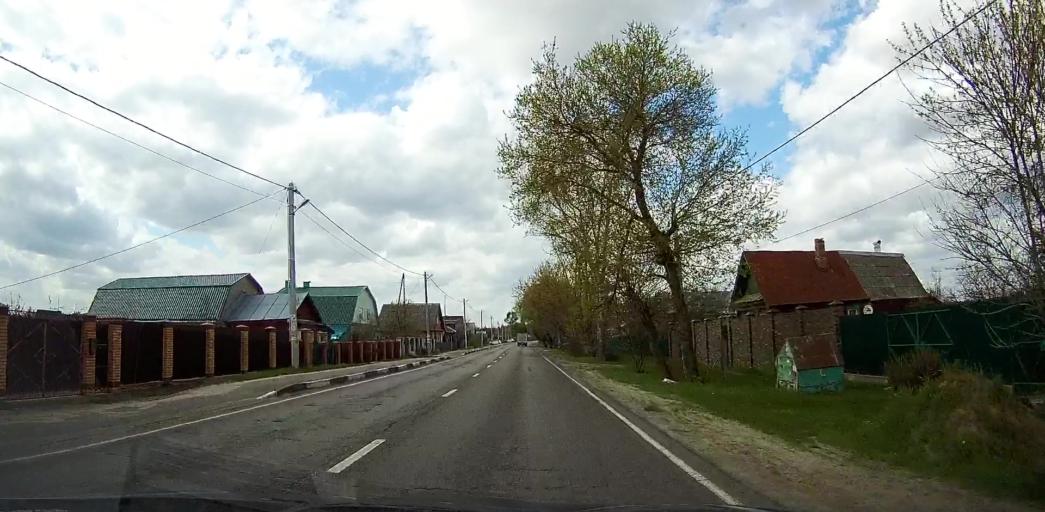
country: RU
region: Moskovskaya
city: Davydovo
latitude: 55.6392
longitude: 38.8640
